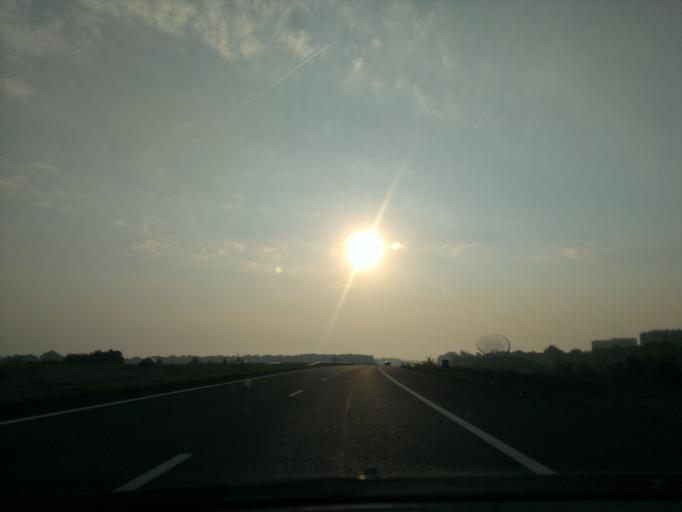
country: NL
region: Drenthe
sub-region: Gemeente Hoogeveen
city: Hoogeveen
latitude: 52.7159
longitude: 6.5146
